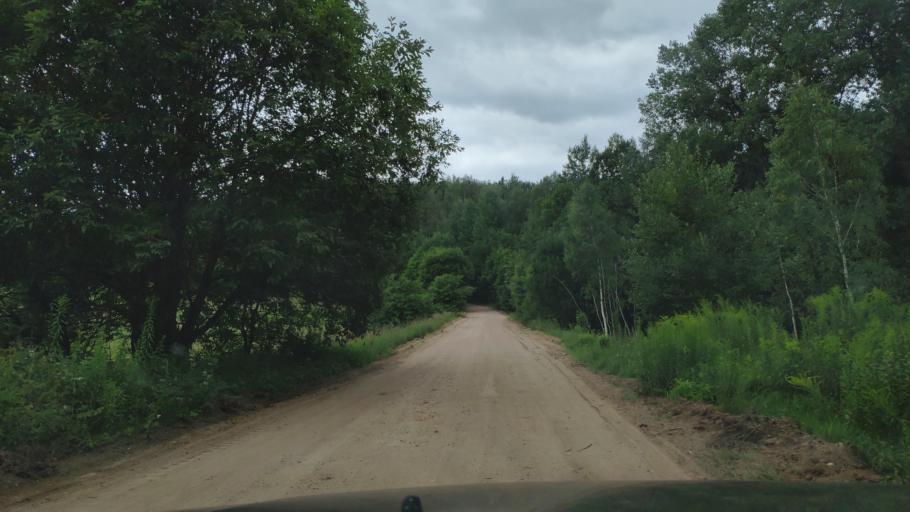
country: BY
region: Minsk
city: Khatsyezhyna
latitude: 53.9353
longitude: 27.2703
